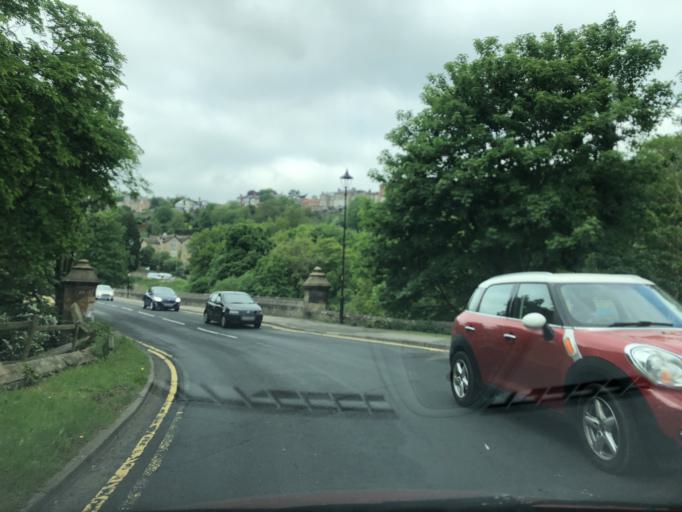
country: GB
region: England
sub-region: North Yorkshire
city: Catterick Garrison
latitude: 54.4033
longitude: -1.7302
